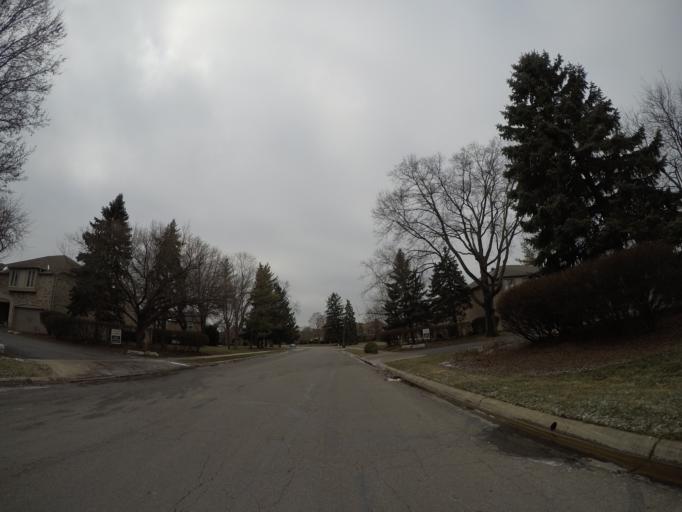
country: US
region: Ohio
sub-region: Franklin County
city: Upper Arlington
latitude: 40.0517
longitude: -83.0617
